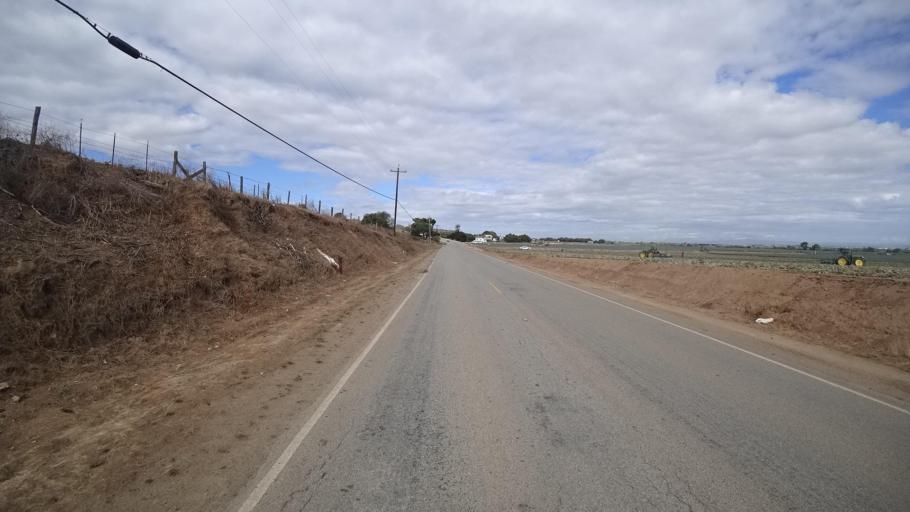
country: US
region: California
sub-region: Monterey County
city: Salinas
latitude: 36.5949
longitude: -121.6184
